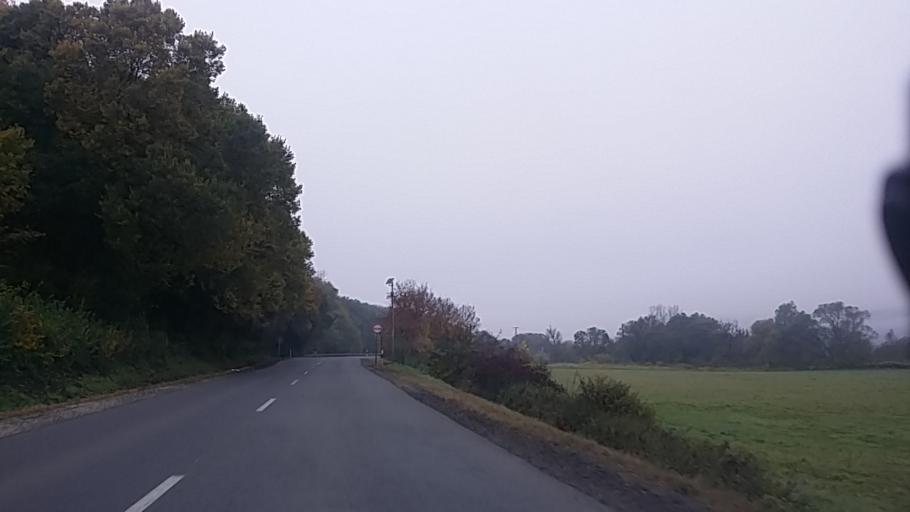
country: HU
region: Borsod-Abauj-Zemplen
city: Sajokaza
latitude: 48.2707
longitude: 20.5353
